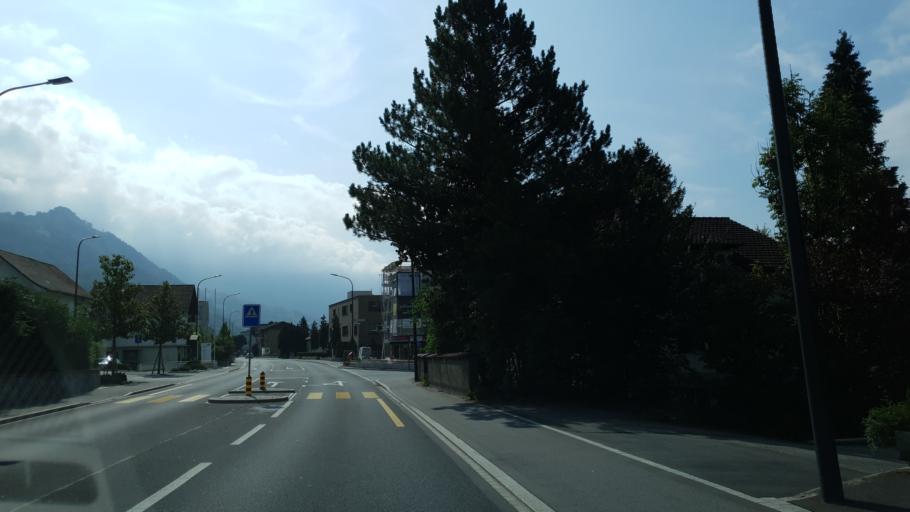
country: LI
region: Vaduz
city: Vaduz
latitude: 47.1480
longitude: 9.5127
